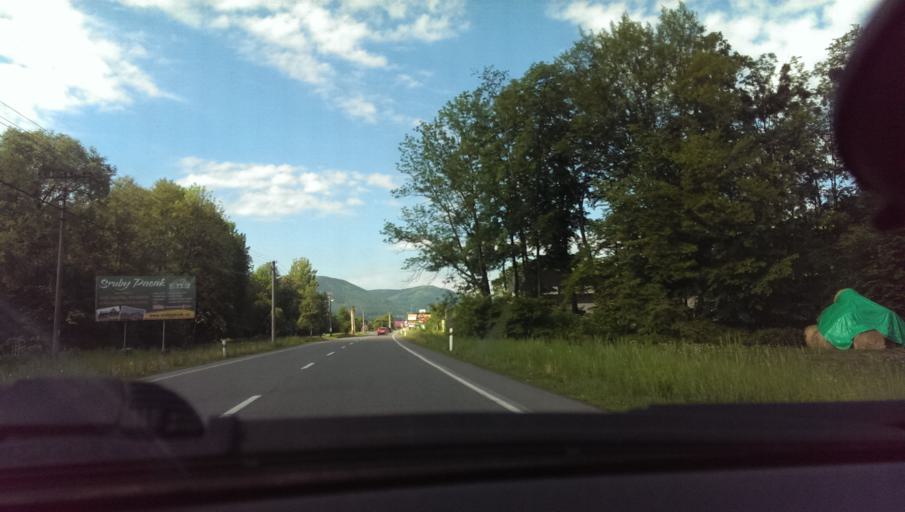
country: CZ
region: Moravskoslezsky
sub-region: Okres Frydek-Mistek
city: Celadna
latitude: 49.5596
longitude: 18.3482
